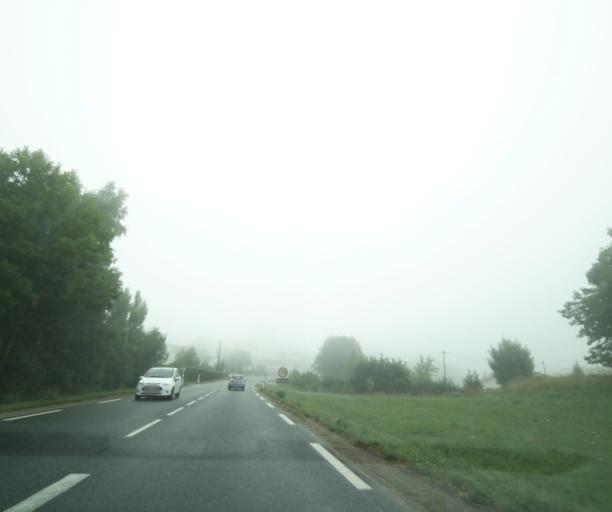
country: FR
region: Midi-Pyrenees
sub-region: Departement de l'Aveyron
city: Baraqueville
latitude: 44.2693
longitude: 2.4197
